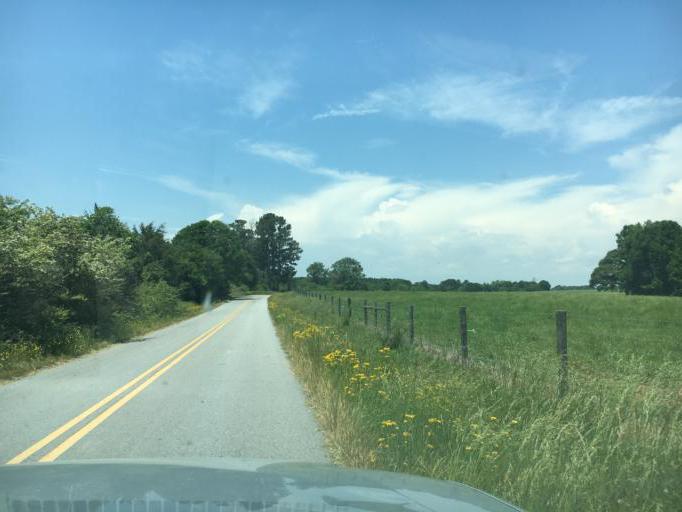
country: US
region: Georgia
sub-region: Hart County
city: Royston
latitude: 34.3193
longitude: -83.1002
